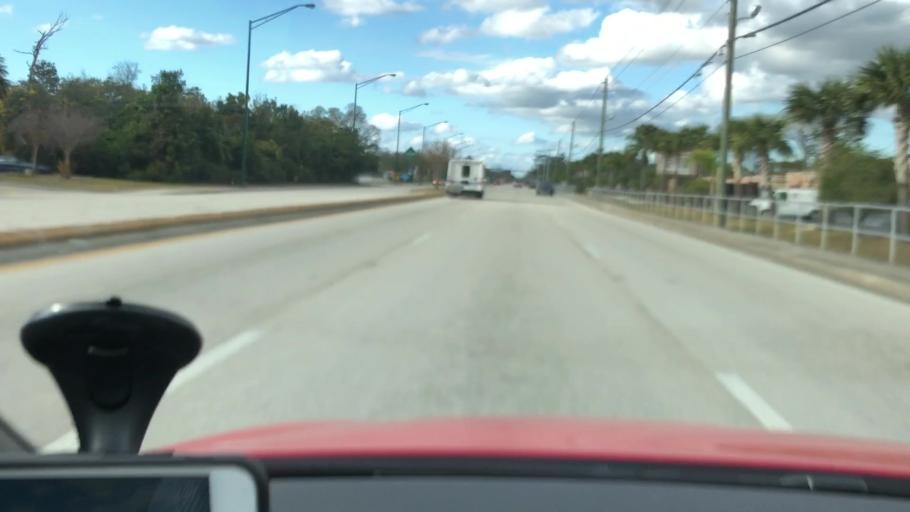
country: US
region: Florida
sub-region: Volusia County
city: Ormond Beach
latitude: 29.2604
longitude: -81.0752
